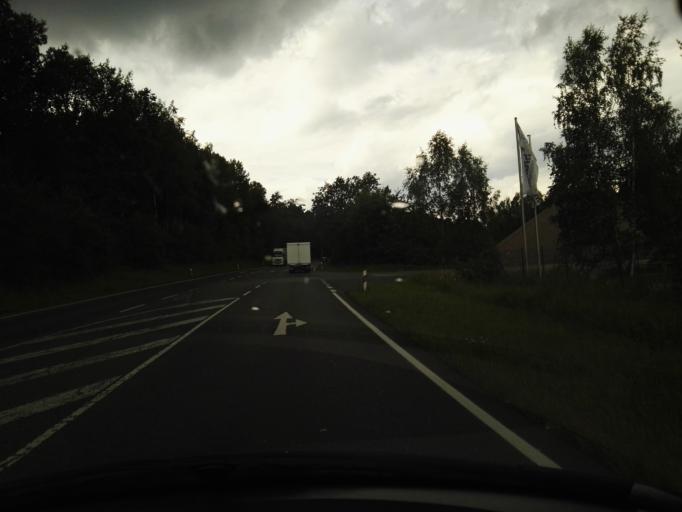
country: DE
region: Bavaria
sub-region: Upper Franconia
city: Michelau
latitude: 50.1505
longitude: 11.1274
